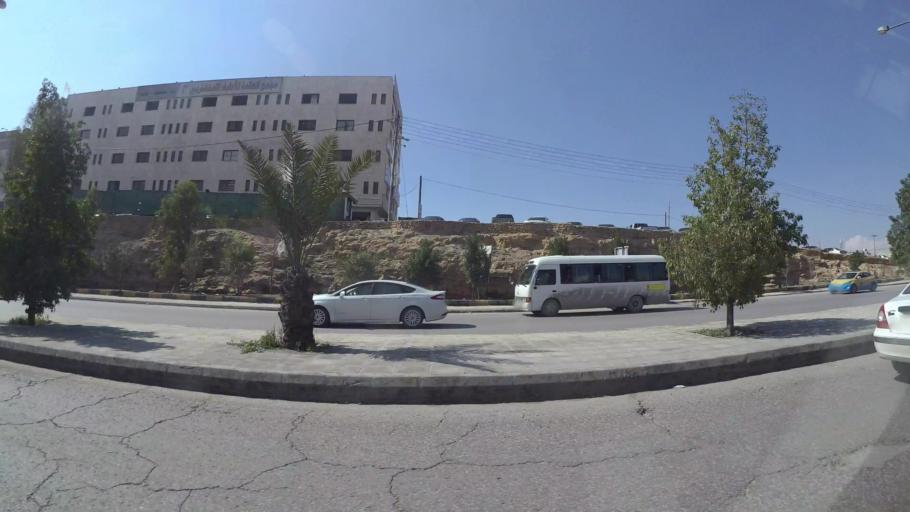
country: JO
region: Zarqa
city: Zarqa
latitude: 32.0541
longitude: 36.0945
